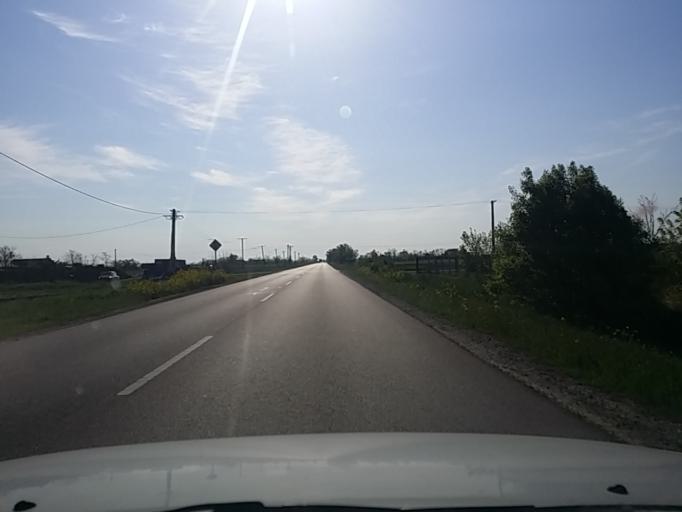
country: HU
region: Jasz-Nagykun-Szolnok
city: Mezotur
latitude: 46.9975
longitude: 20.6695
